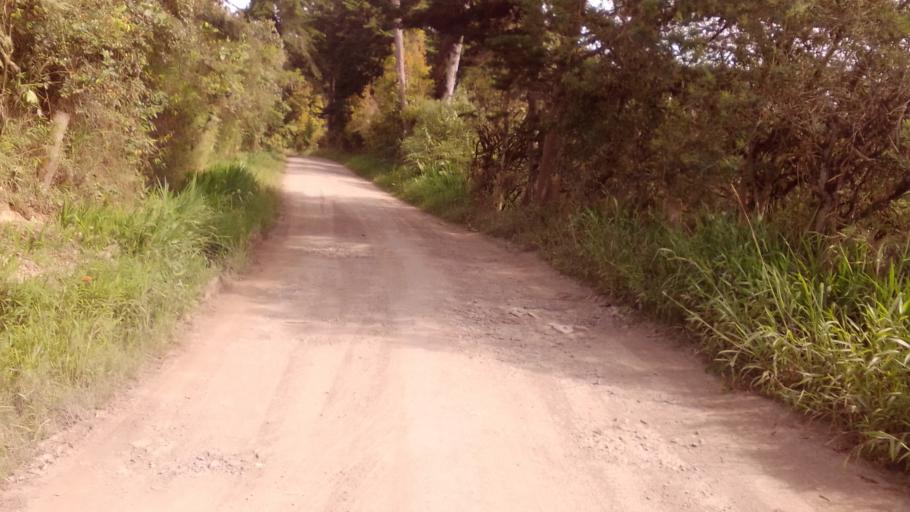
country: CO
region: Cundinamarca
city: Tenza
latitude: 5.1008
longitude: -73.4167
